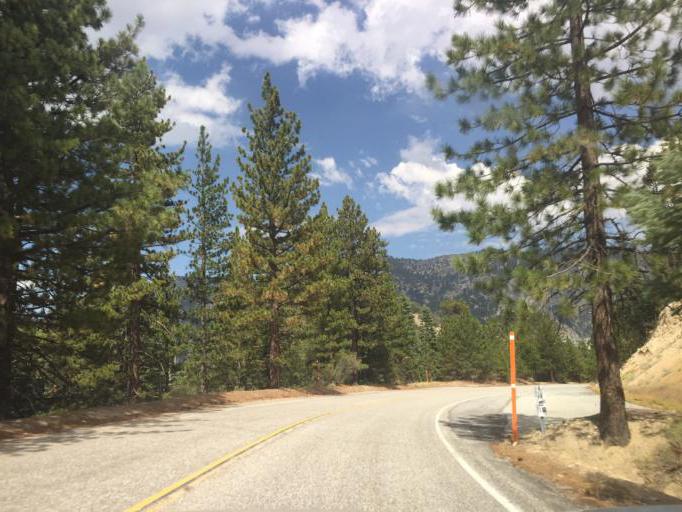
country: US
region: California
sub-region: Los Angeles County
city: Littlerock
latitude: 34.3533
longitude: -117.8804
